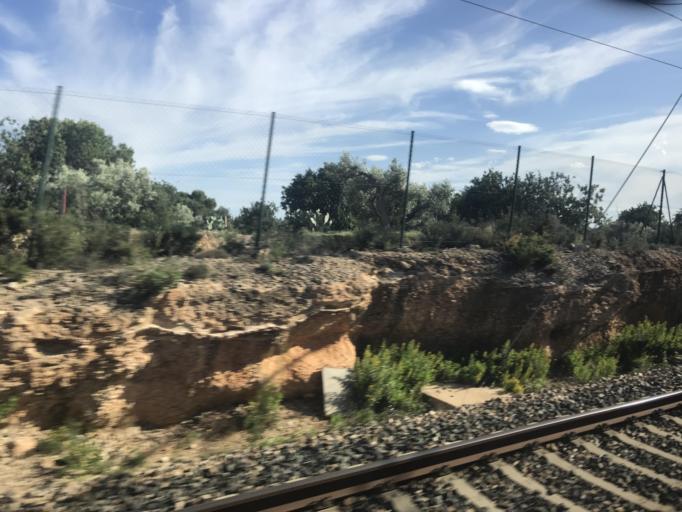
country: ES
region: Catalonia
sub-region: Provincia de Tarragona
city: l'Ametlla de Mar
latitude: 40.8629
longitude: 0.7742
